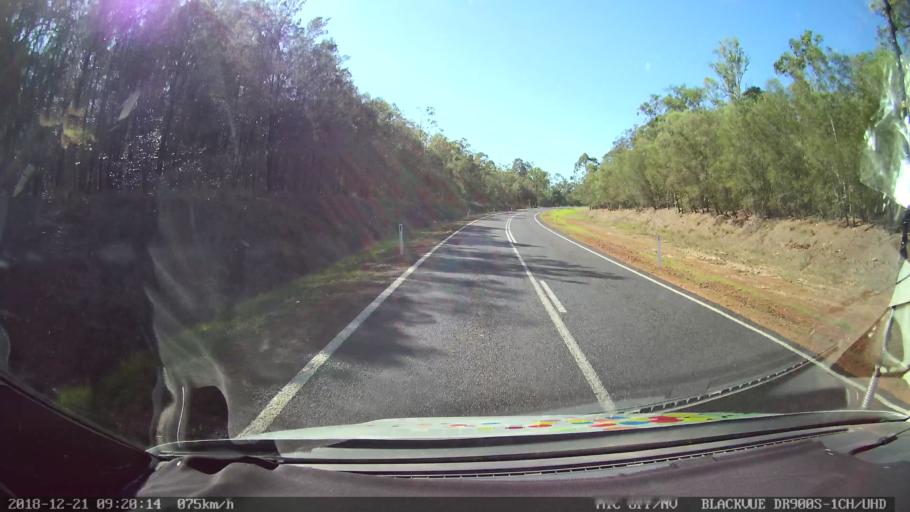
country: AU
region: New South Wales
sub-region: Clarence Valley
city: Maclean
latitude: -29.3125
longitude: 152.9999
